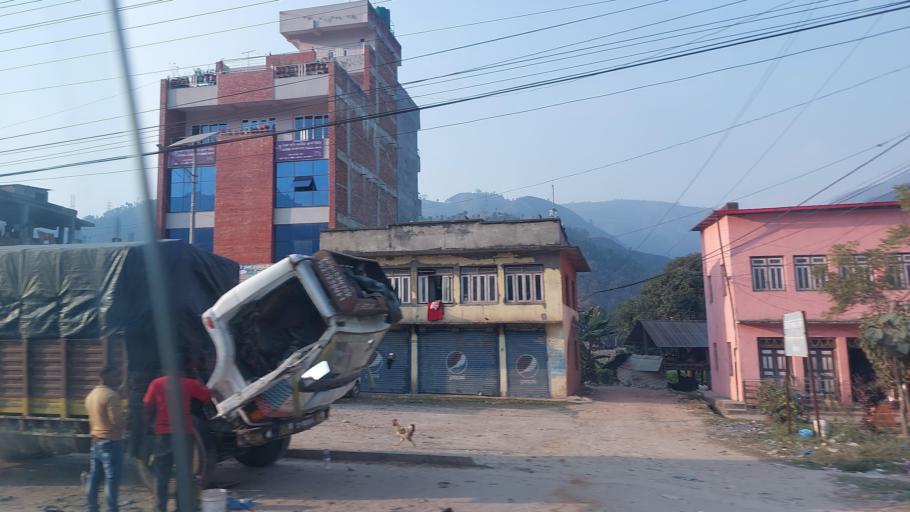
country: NP
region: Central Region
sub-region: Narayani Zone
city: Hitura
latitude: 27.8050
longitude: 84.8790
